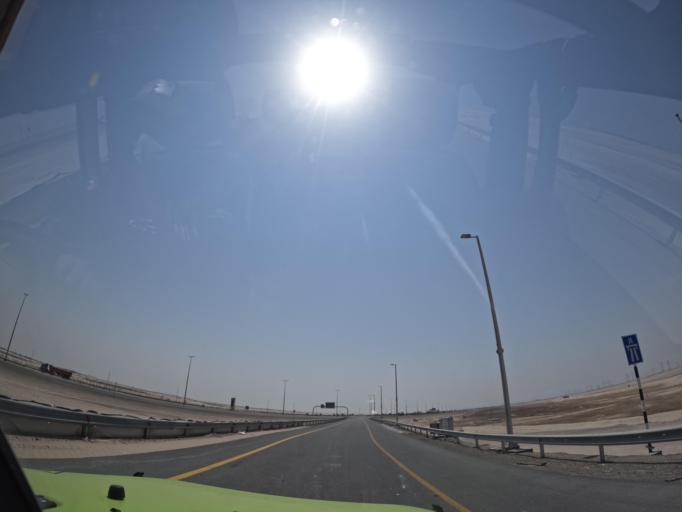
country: AE
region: Abu Dhabi
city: Abu Dhabi
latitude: 24.2442
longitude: 54.4690
